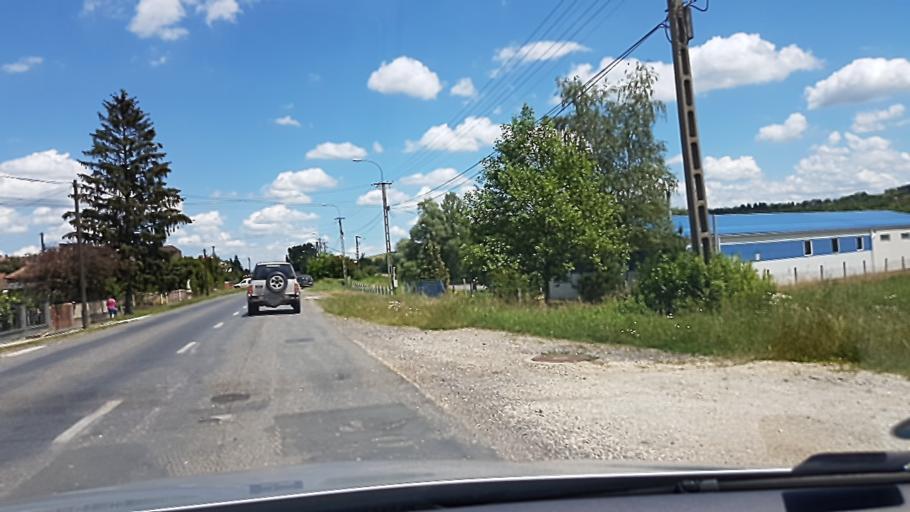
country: HU
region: Zala
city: Zalaegerszeg
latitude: 46.8465
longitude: 16.7715
